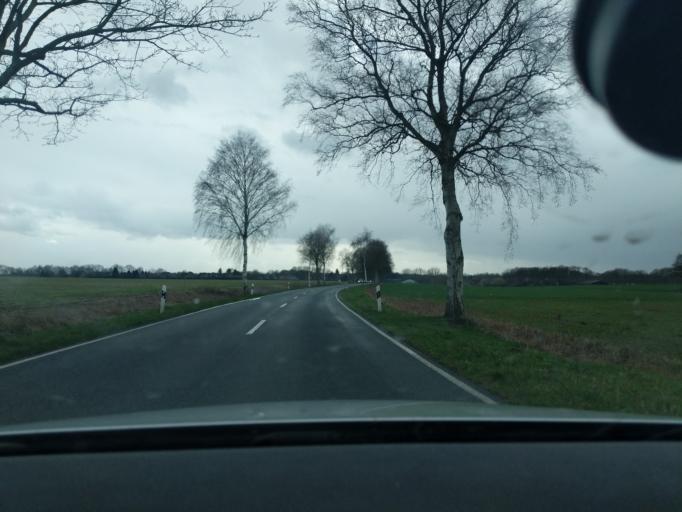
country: DE
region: Lower Saxony
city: Bliedersdorf
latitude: 53.4926
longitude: 9.5289
